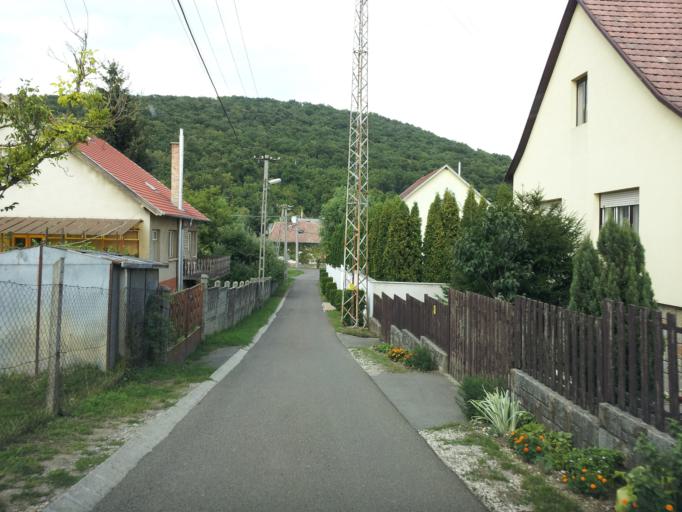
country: HU
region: Pest
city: Kismaros
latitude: 47.8295
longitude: 19.0092
